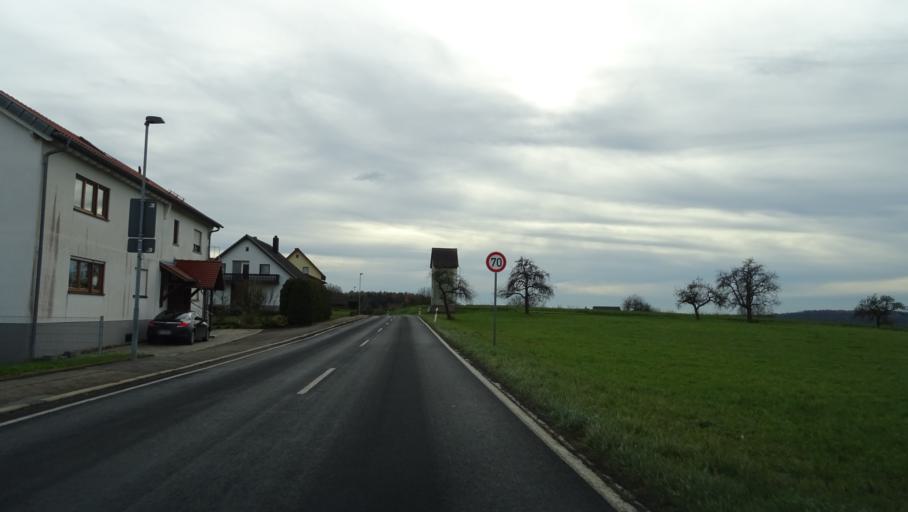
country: DE
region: Baden-Wuerttemberg
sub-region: Karlsruhe Region
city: Fahrenbach
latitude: 49.4113
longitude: 9.1572
